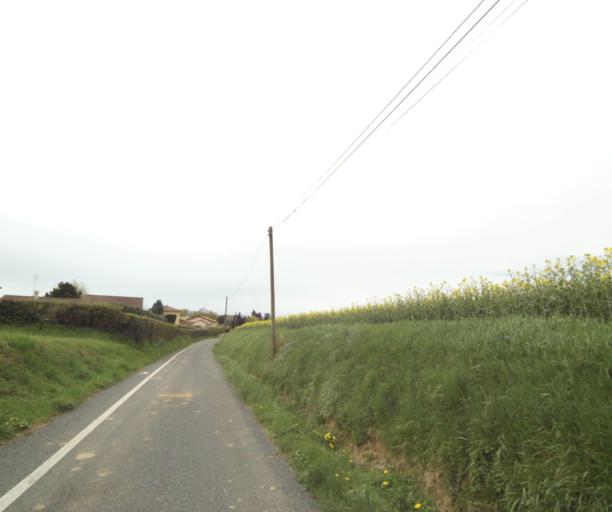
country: FR
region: Bourgogne
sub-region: Departement de Saone-et-Loire
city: Charnay-les-Macon
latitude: 46.3126
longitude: 4.8017
